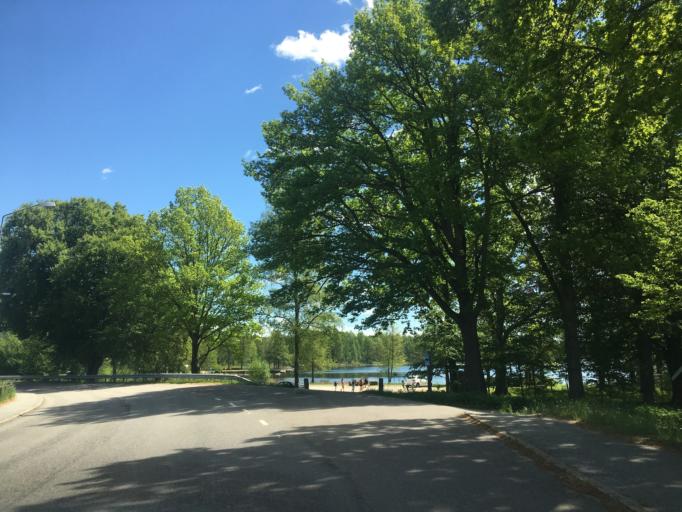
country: SE
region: Blekinge
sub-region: Olofstroms Kommun
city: Olofstroem
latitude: 56.3530
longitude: 14.5914
